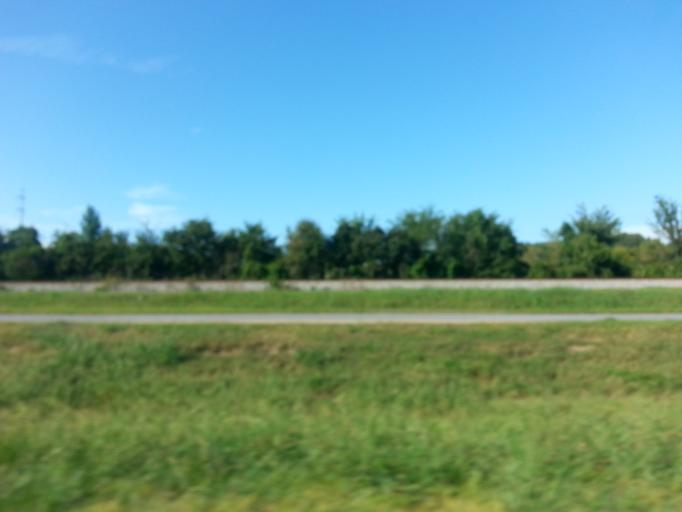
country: US
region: Alabama
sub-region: Colbert County
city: Tuscumbia
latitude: 34.7203
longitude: -87.8036
